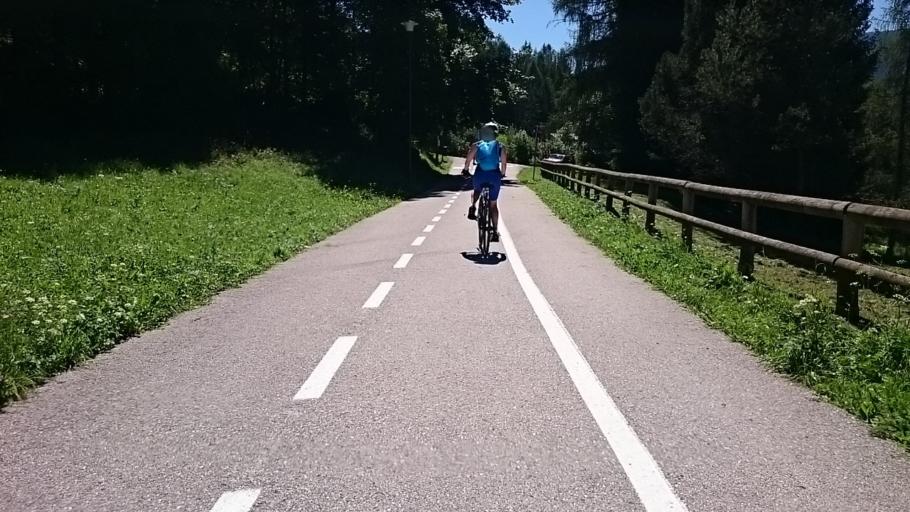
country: IT
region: Veneto
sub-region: Provincia di Belluno
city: San Vito
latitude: 46.4515
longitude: 12.2117
